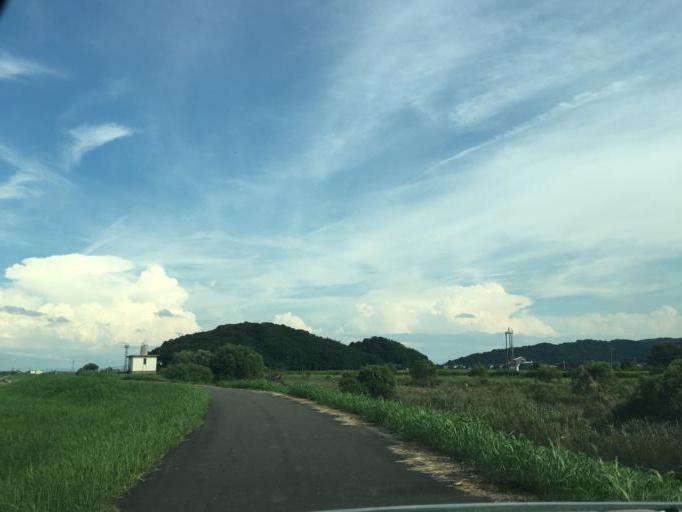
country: JP
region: Saga Prefecture
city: Takeocho-takeo
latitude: 33.2137
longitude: 130.0750
